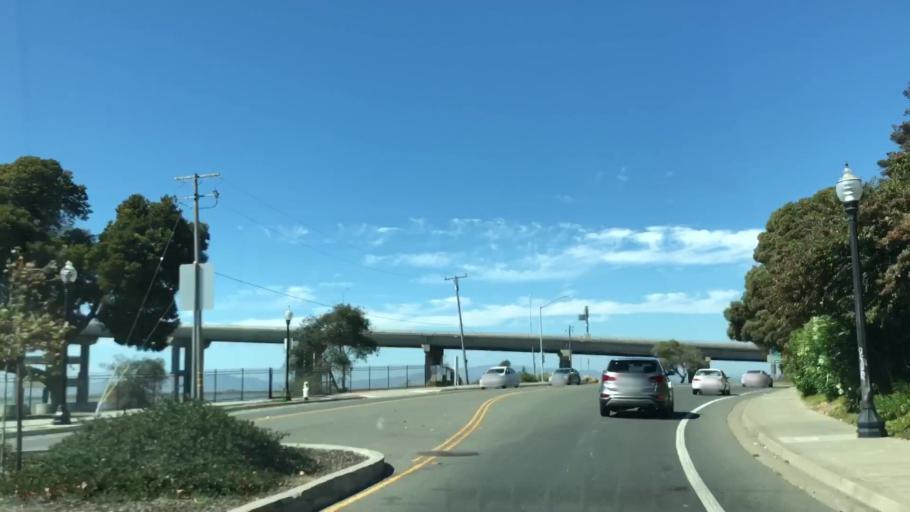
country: US
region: California
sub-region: Solano County
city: Vallejo
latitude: 38.1201
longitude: -122.2753
